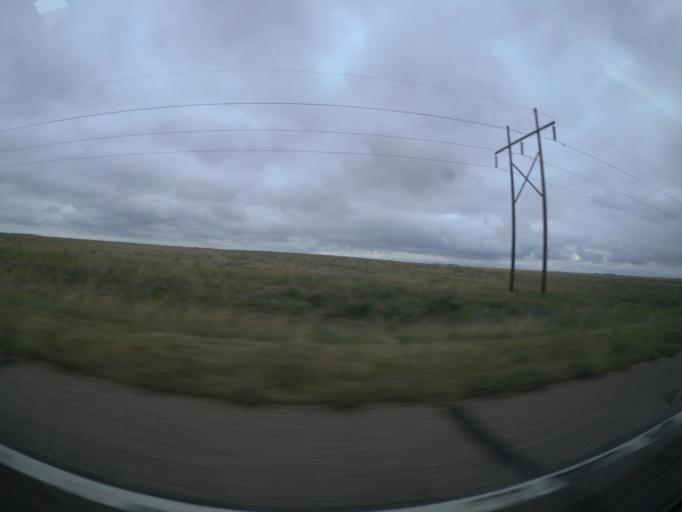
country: US
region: Colorado
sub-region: Yuma County
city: Yuma
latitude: 39.6550
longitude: -102.7898
